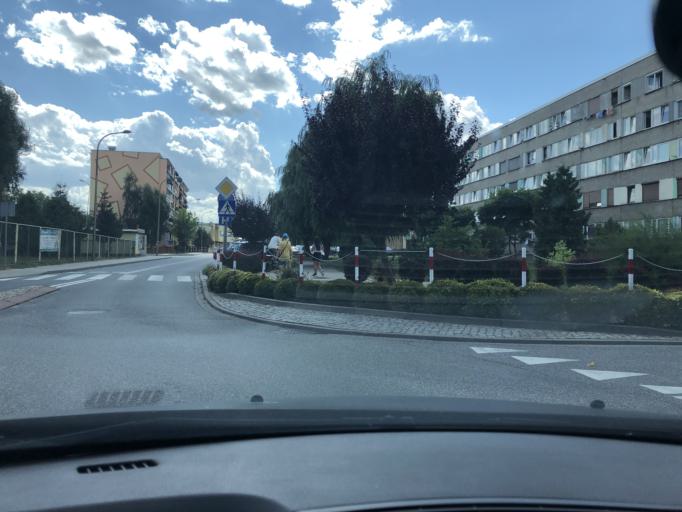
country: PL
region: Lodz Voivodeship
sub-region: Powiat wieruszowski
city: Wieruszow
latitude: 51.2966
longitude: 18.1635
